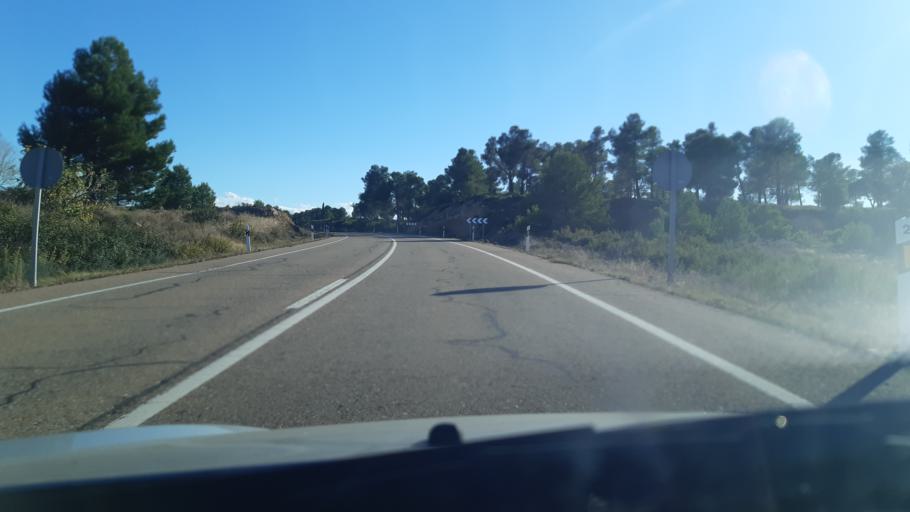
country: ES
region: Aragon
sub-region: Provincia de Teruel
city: Valjunquera
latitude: 40.9426
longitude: -0.0121
